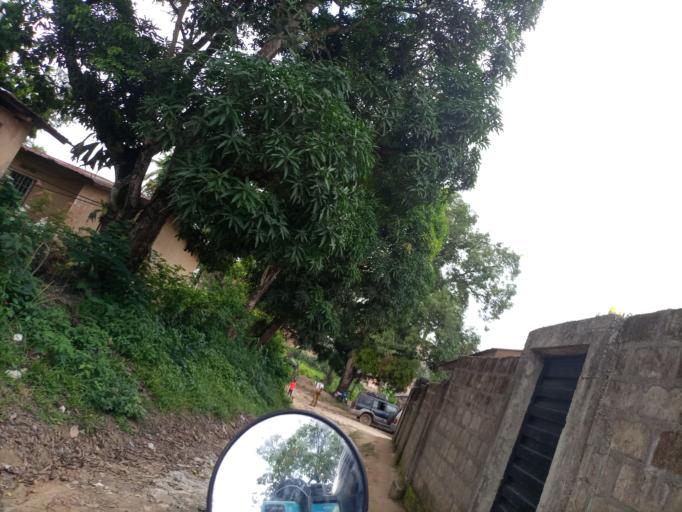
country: SL
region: Southern Province
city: Bo
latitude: 7.9477
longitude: -11.7315
